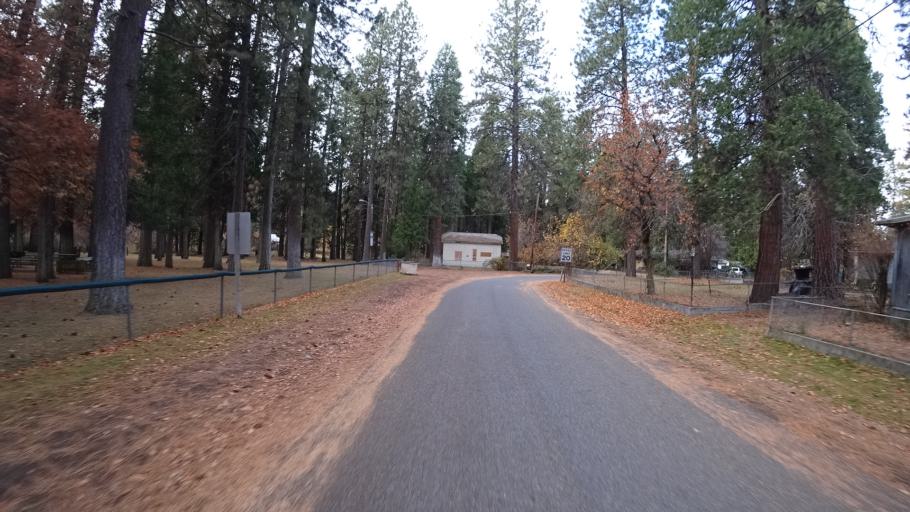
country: US
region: California
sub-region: Siskiyou County
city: Weed
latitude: 41.4450
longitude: -122.3643
